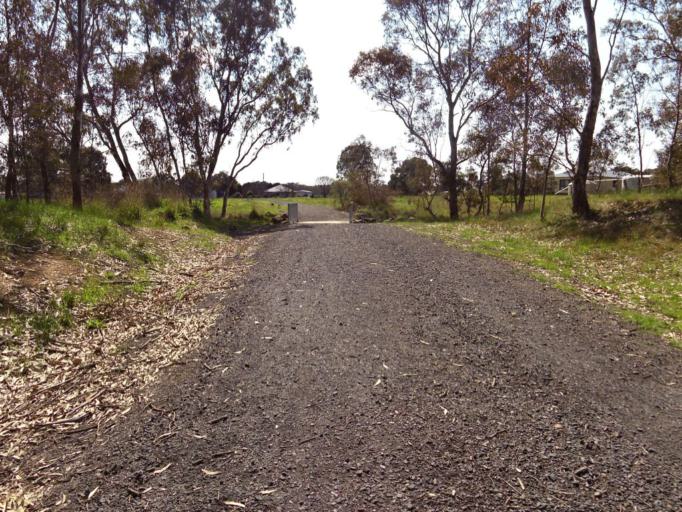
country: AU
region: Victoria
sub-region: Murrindindi
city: Alexandra
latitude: -37.1029
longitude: 145.6180
